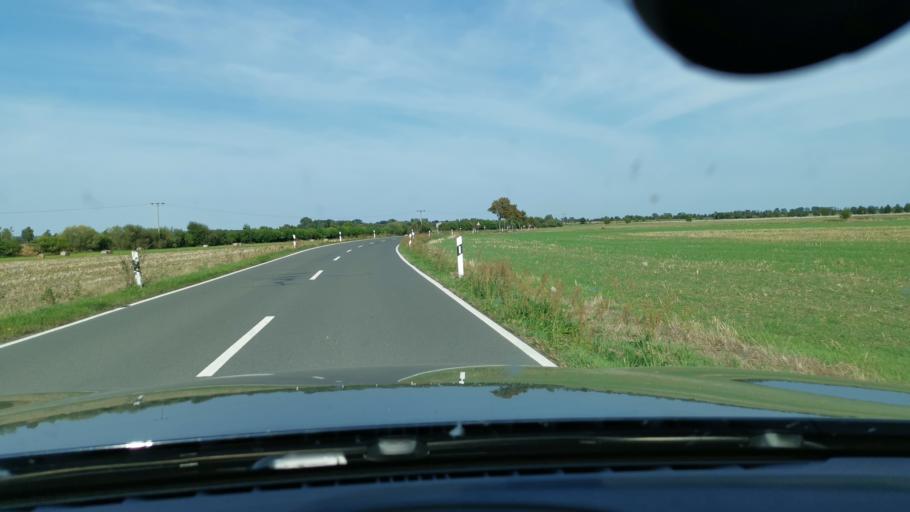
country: DE
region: Saxony
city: Mockrehna
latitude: 51.4771
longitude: 12.8145
